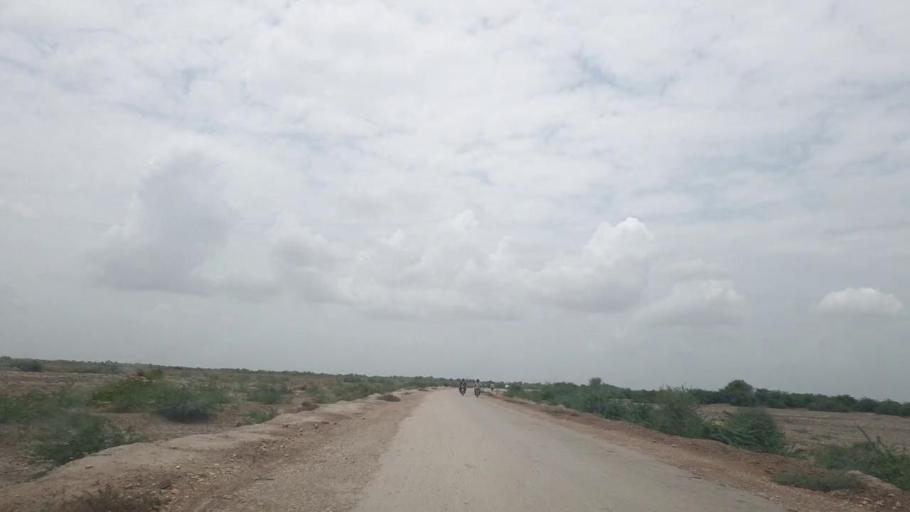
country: PK
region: Sindh
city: Naukot
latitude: 24.9514
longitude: 69.2823
